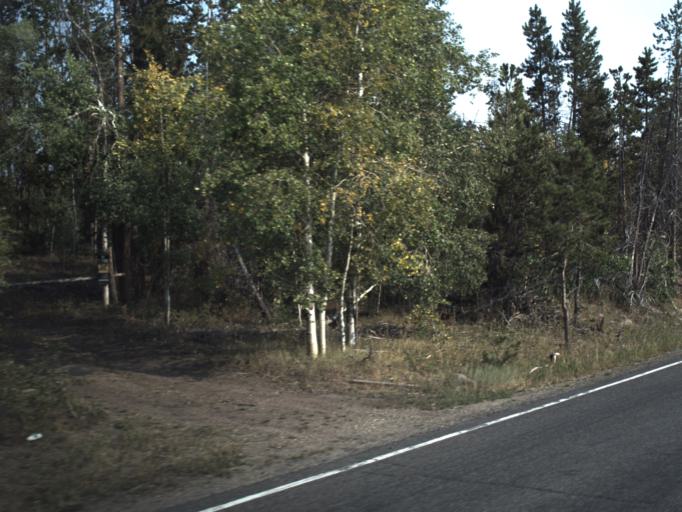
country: US
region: Wyoming
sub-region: Uinta County
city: Evanston
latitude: 40.9228
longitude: -110.8275
